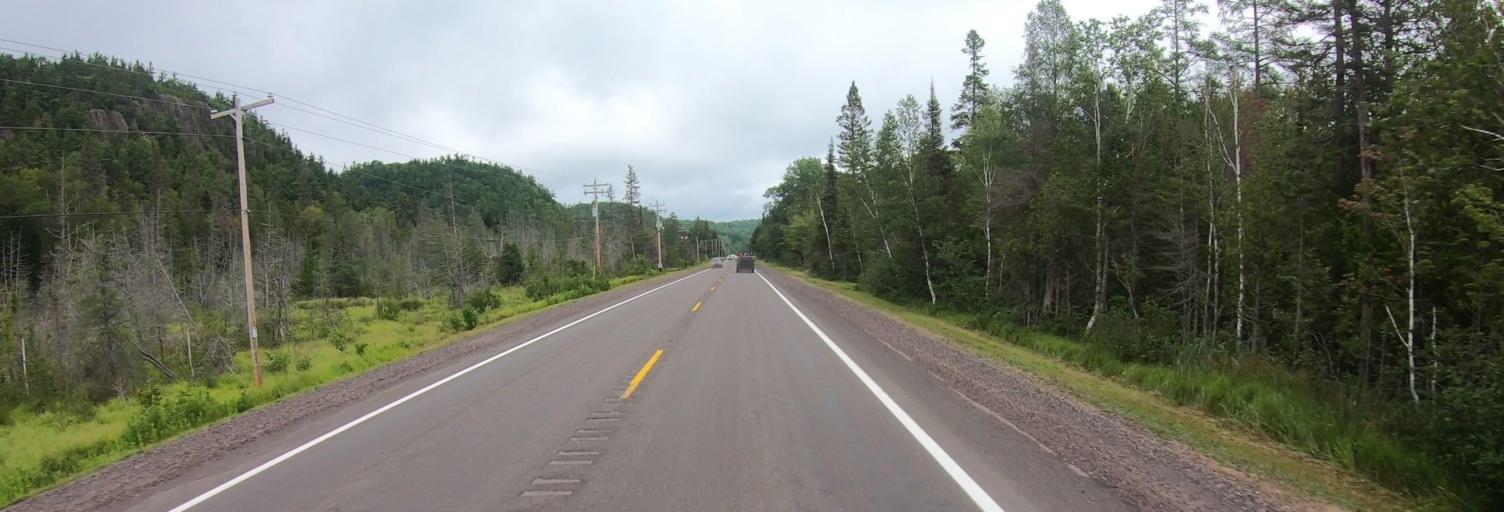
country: US
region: Michigan
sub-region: Keweenaw County
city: Eagle River
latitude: 47.3838
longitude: -88.2922
